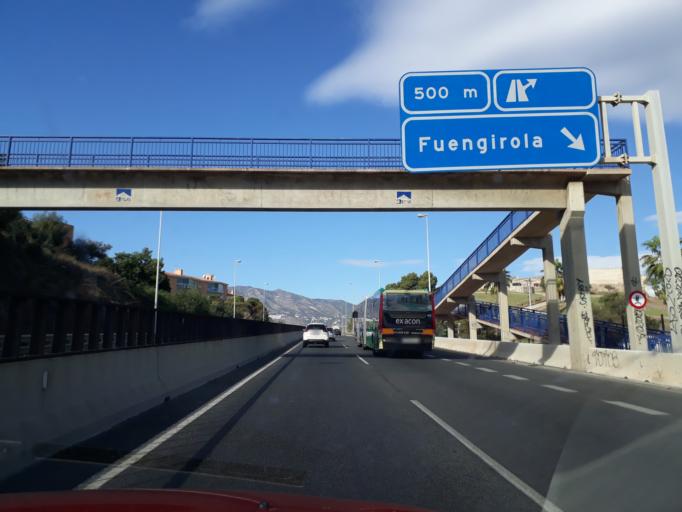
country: ES
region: Andalusia
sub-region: Provincia de Malaga
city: Fuengirola
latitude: 36.5232
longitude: -4.6301
